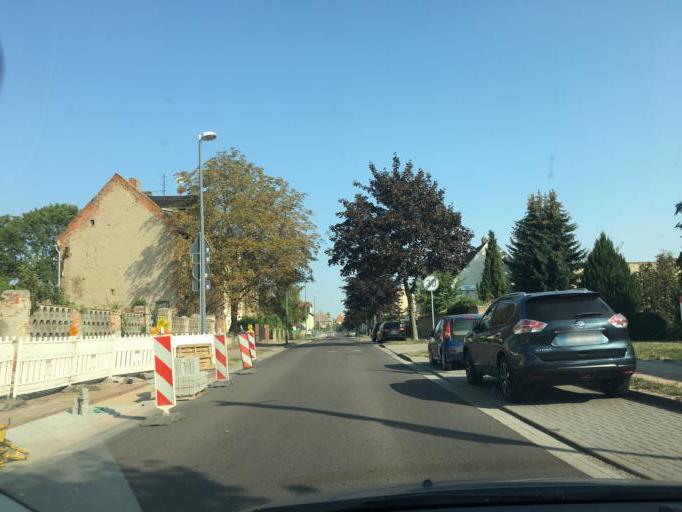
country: DE
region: Saxony-Anhalt
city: Nienburg/Saale
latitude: 51.8440
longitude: 11.7673
